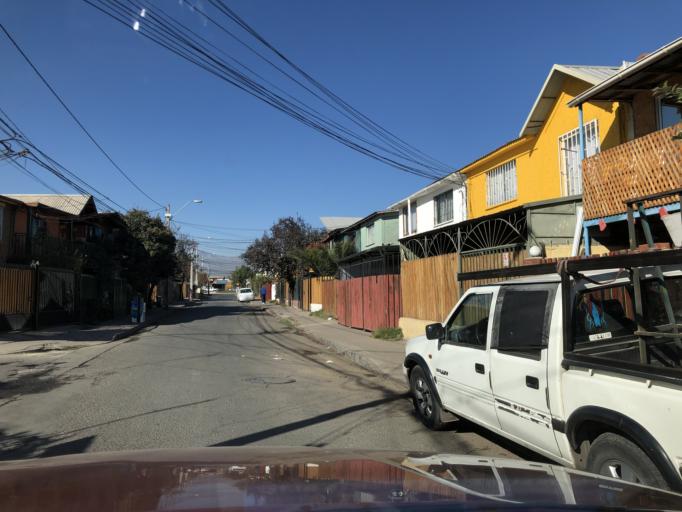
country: CL
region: Santiago Metropolitan
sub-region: Provincia de Cordillera
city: Puente Alto
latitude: -33.5954
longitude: -70.5635
